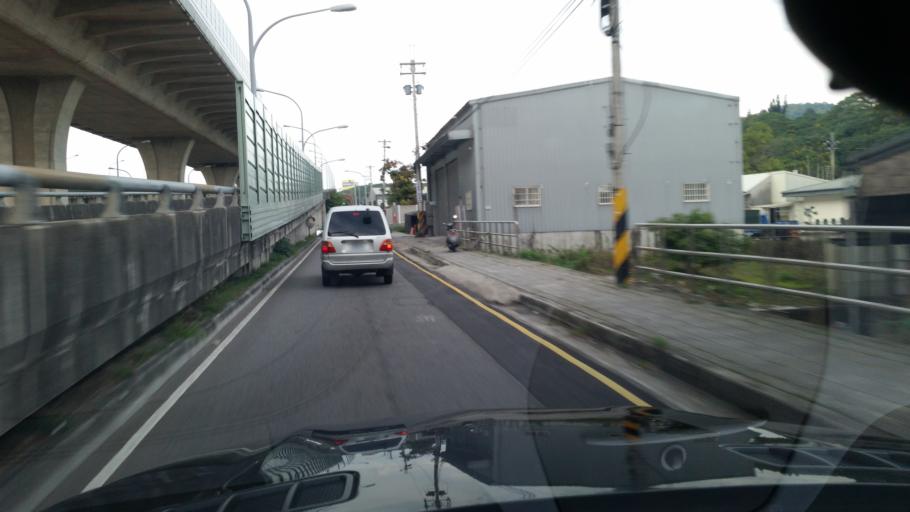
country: TW
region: Taiwan
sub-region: Taichung City
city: Taichung
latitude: 24.1840
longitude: 120.7222
